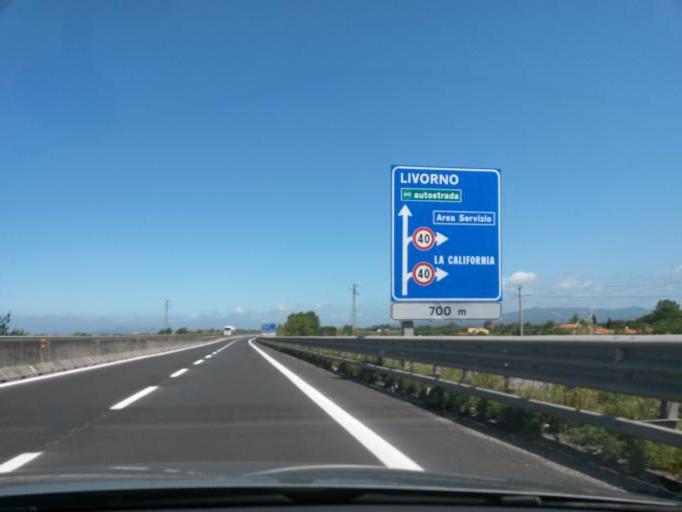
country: IT
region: Tuscany
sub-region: Provincia di Livorno
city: La California
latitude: 43.2723
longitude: 10.5398
